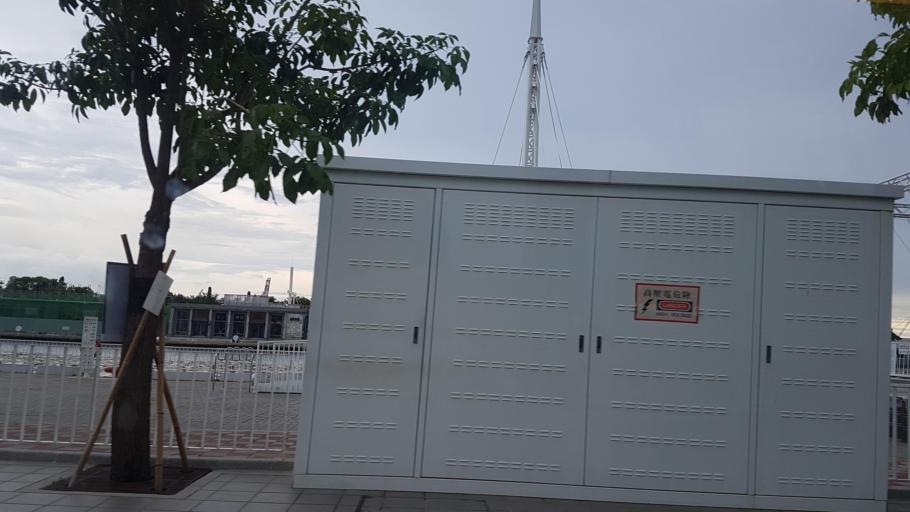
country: TW
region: Kaohsiung
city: Kaohsiung
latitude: 22.6183
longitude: 120.2845
